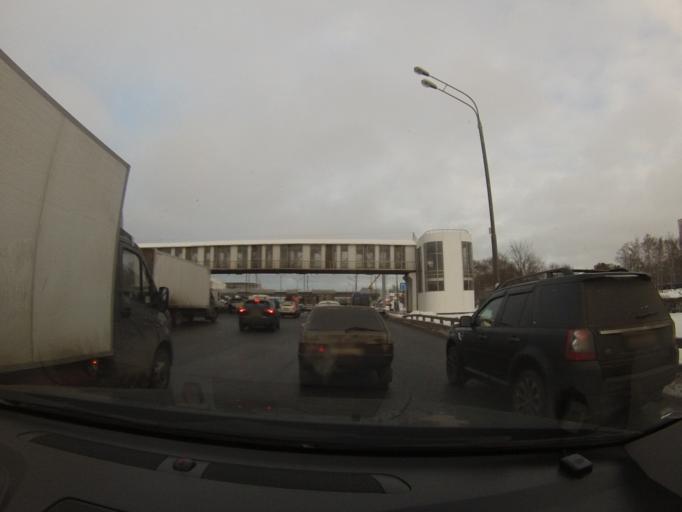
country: RU
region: Moskovskaya
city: Marfino
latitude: 55.7172
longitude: 37.3845
